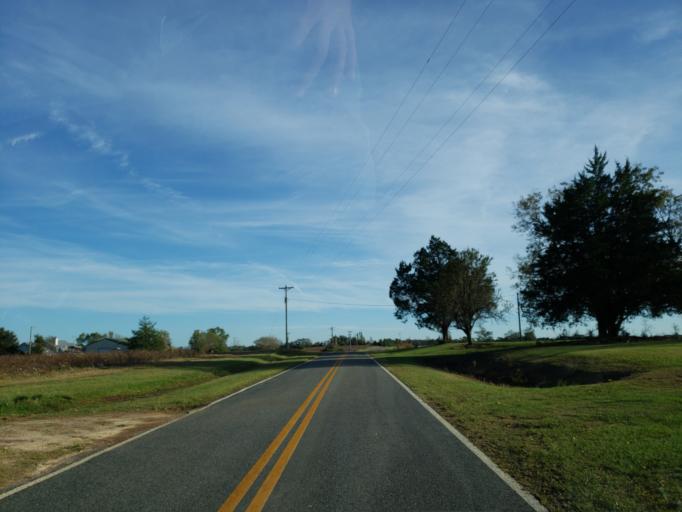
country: US
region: Georgia
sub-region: Dooly County
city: Vienna
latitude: 32.0431
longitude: -83.7548
